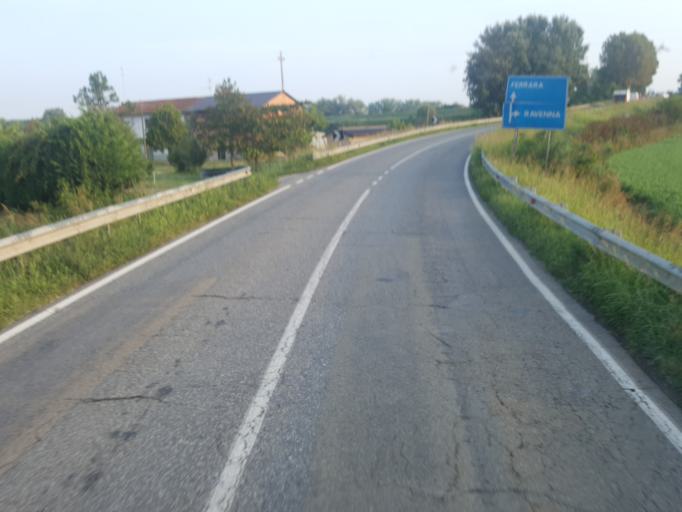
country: IT
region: Emilia-Romagna
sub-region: Provincia di Ravenna
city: Lavezzola
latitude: 44.5740
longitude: 11.8741
